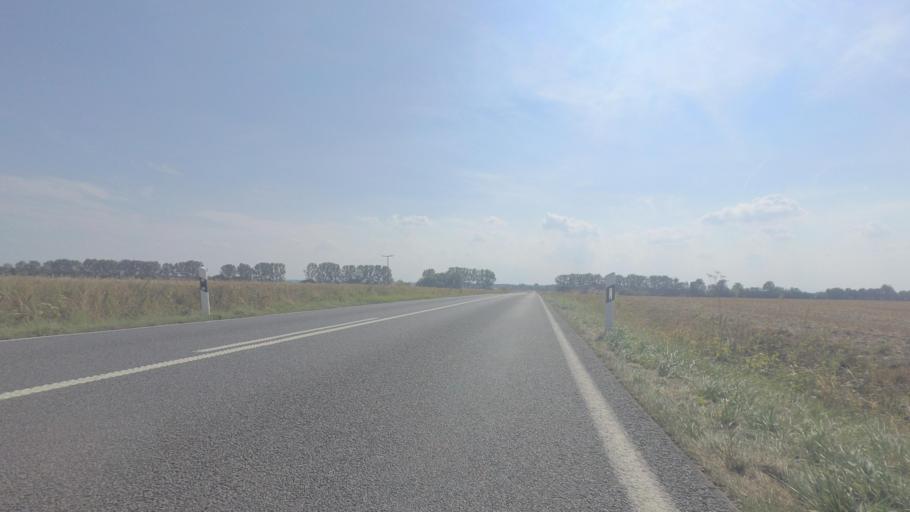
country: DE
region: Mecklenburg-Vorpommern
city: Wittenhagen
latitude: 54.1426
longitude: 13.1503
